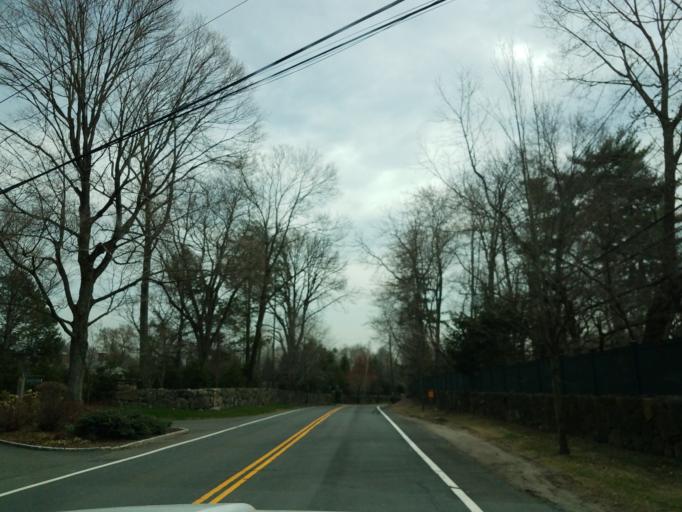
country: US
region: Connecticut
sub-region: Fairfield County
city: Greenwich
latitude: 41.0457
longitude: -73.6363
